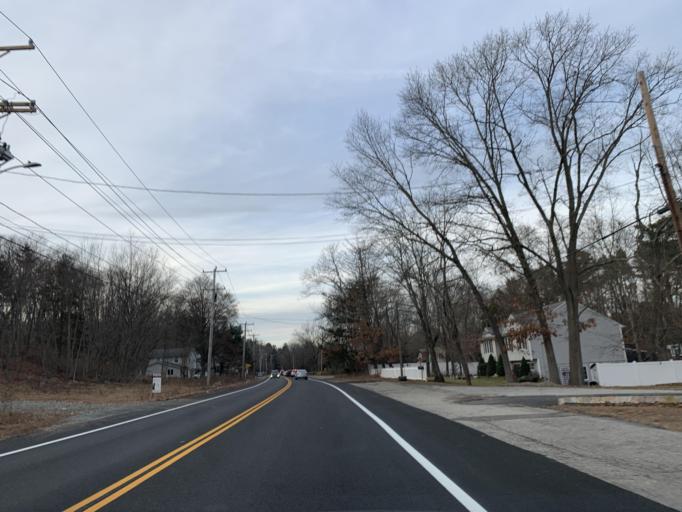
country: US
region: Rhode Island
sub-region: Providence County
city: Greenville
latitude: 41.8582
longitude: -71.5276
